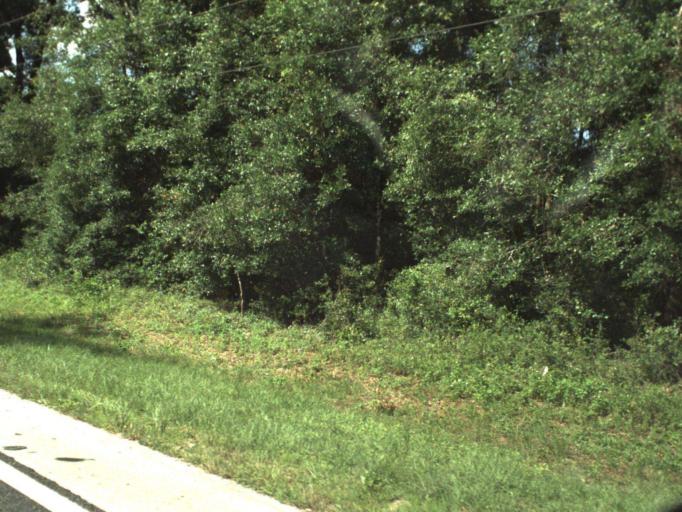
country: US
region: Florida
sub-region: Marion County
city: Belleview
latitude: 29.1020
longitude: -82.0884
